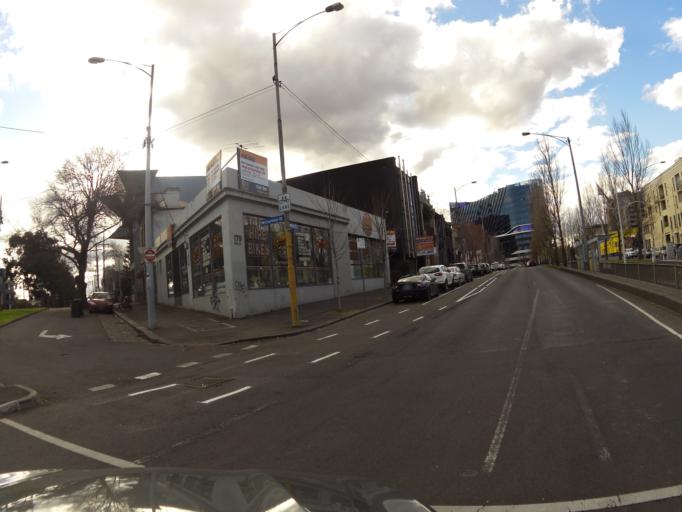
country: AU
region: Victoria
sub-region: Melbourne
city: North Melbourne
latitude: -37.8038
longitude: 144.9563
